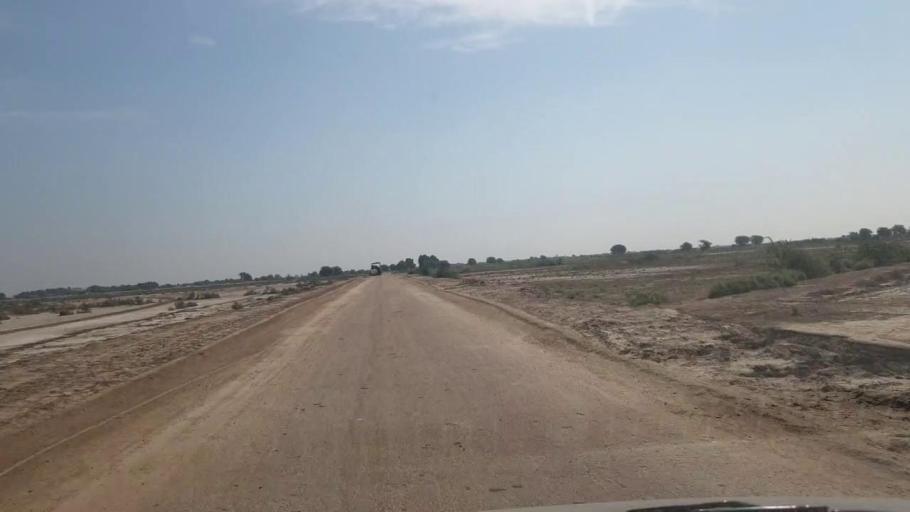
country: PK
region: Sindh
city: Digri
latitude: 24.9743
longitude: 69.1222
